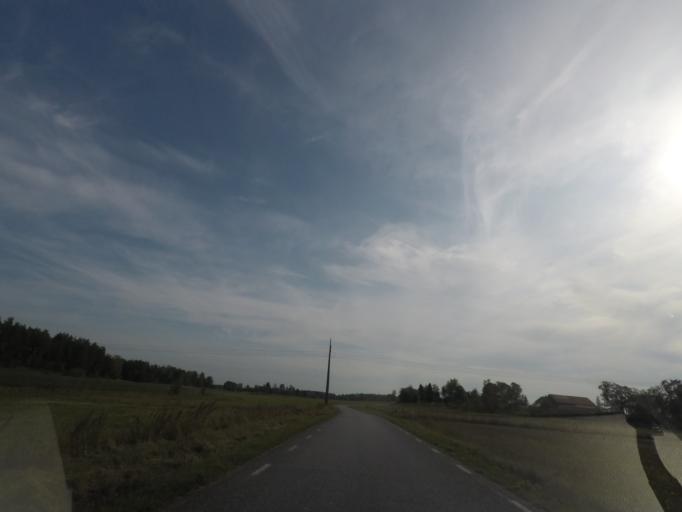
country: SE
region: Vaestmanland
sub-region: Hallstahammars Kommun
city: Kolback
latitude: 59.5303
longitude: 16.1420
